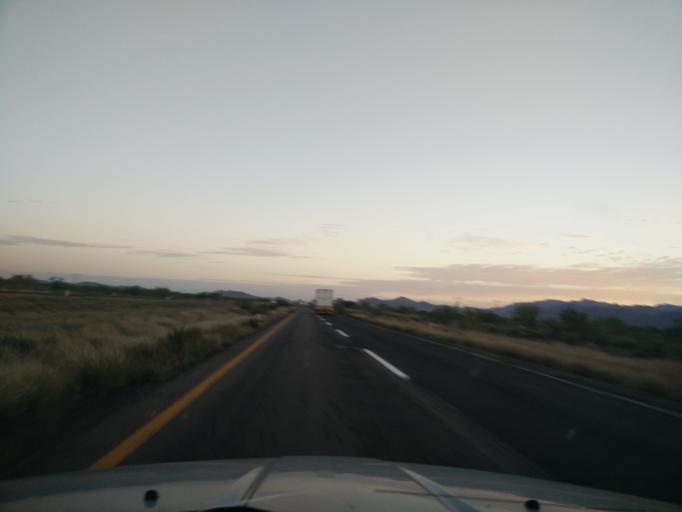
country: MX
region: Sonora
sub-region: Empalme
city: Empalme
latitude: 28.3406
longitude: -111.0423
